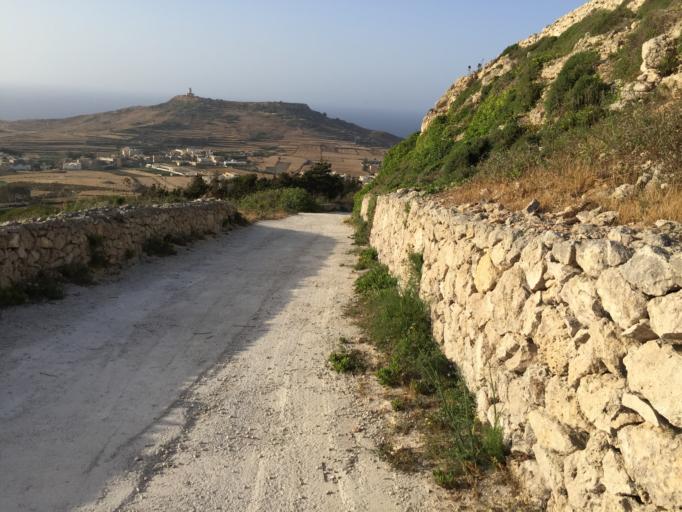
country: MT
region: L-Gharb
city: Gharb
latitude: 36.0595
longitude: 14.2190
